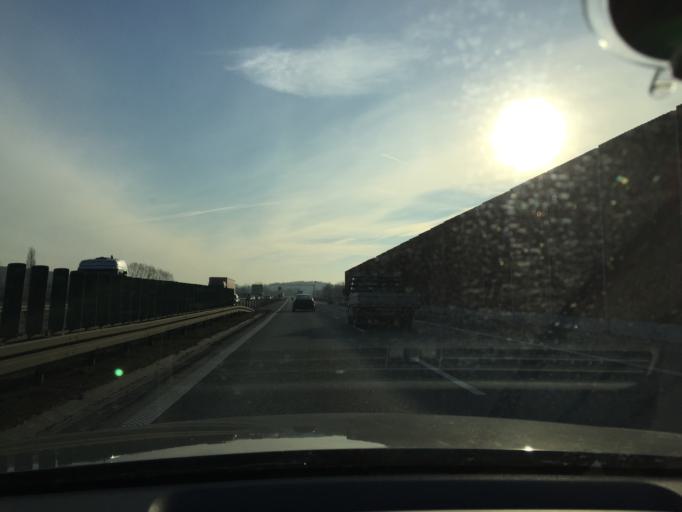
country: PL
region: Lesser Poland Voivodeship
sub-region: Powiat krakowski
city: Kryspinow
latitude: 50.0603
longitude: 19.8095
